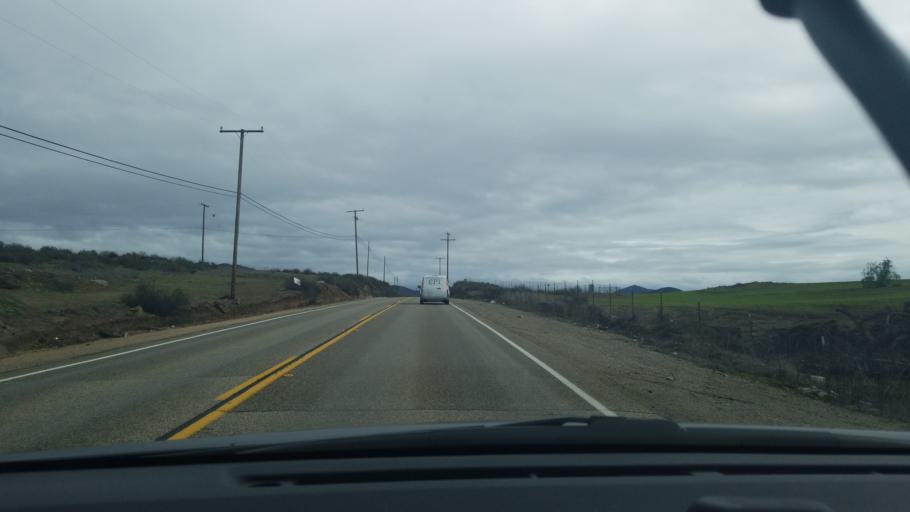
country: US
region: California
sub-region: Riverside County
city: Winchester
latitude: 33.6418
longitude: -117.0941
